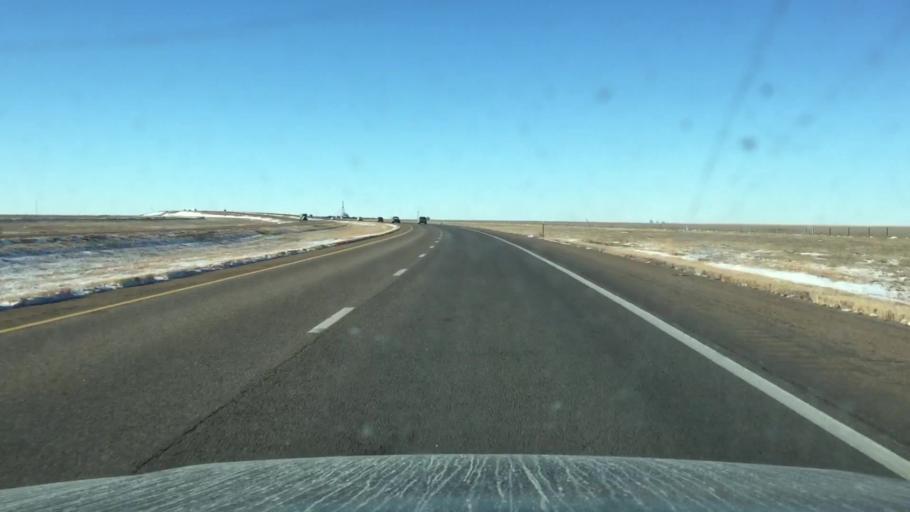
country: US
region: Kansas
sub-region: Thomas County
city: Colby
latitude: 39.3079
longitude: -100.9665
